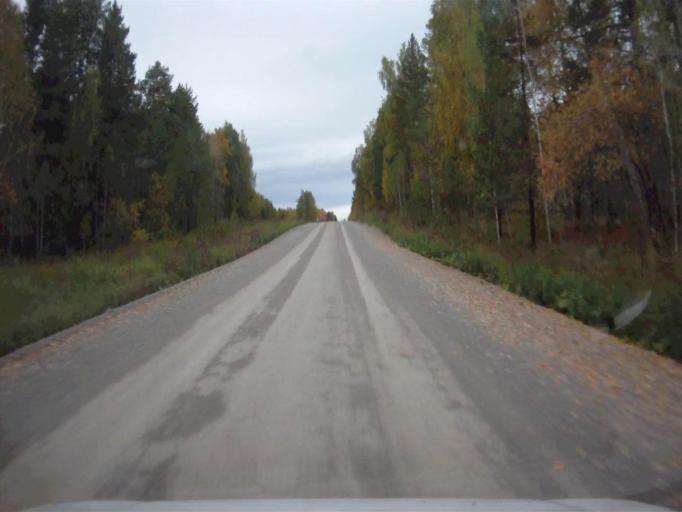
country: RU
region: Chelyabinsk
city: Nyazepetrovsk
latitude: 56.0782
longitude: 59.4247
